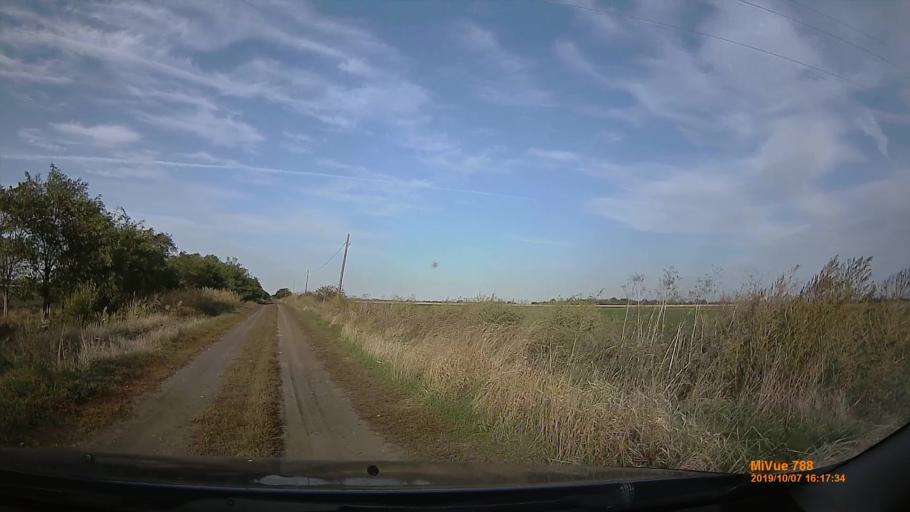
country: HU
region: Bekes
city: Szarvas
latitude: 46.8054
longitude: 20.6217
